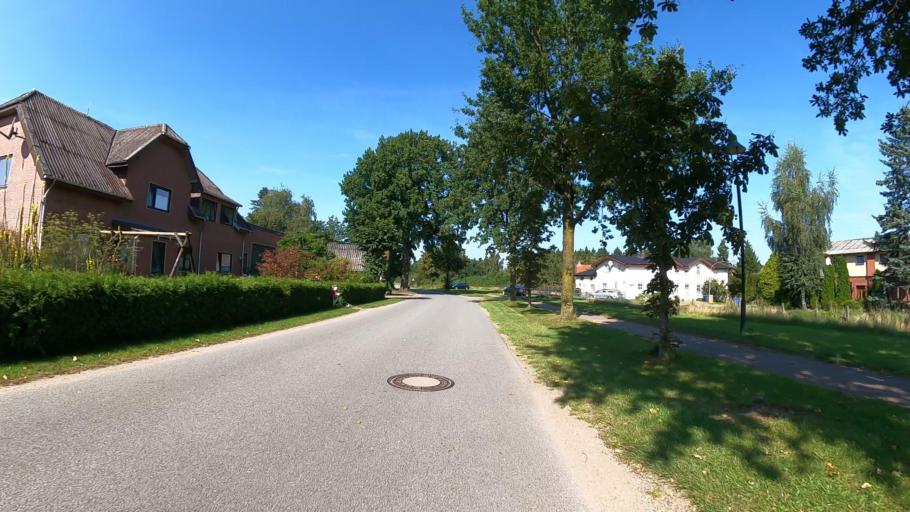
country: DE
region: Schleswig-Holstein
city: Nutzen
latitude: 53.8643
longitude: 9.9160
